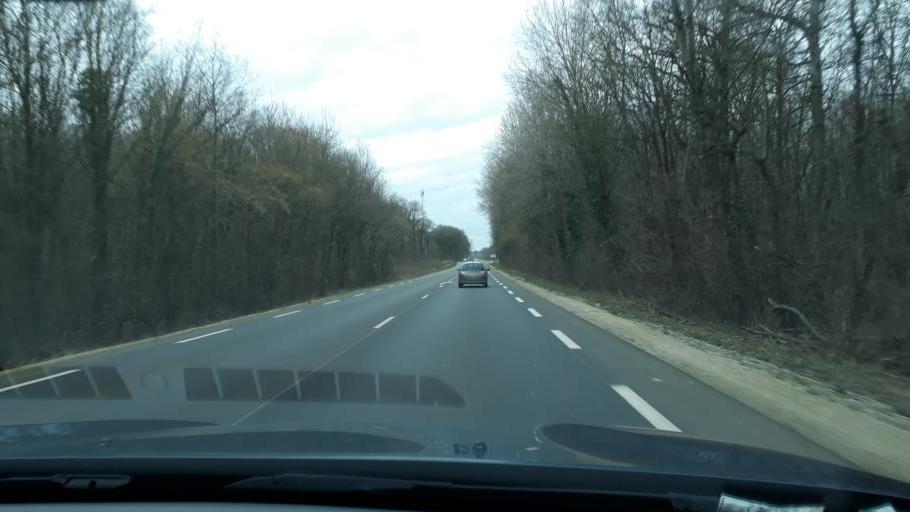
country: FR
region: Centre
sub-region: Departement du Loiret
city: Chanteau
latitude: 48.0121
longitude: 1.9569
